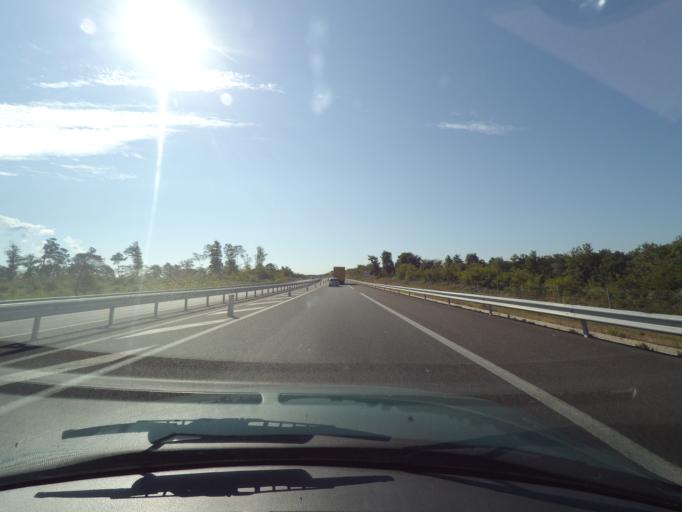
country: FR
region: Poitou-Charentes
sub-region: Departement de la Vienne
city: Terce
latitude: 46.4607
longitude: 0.5516
